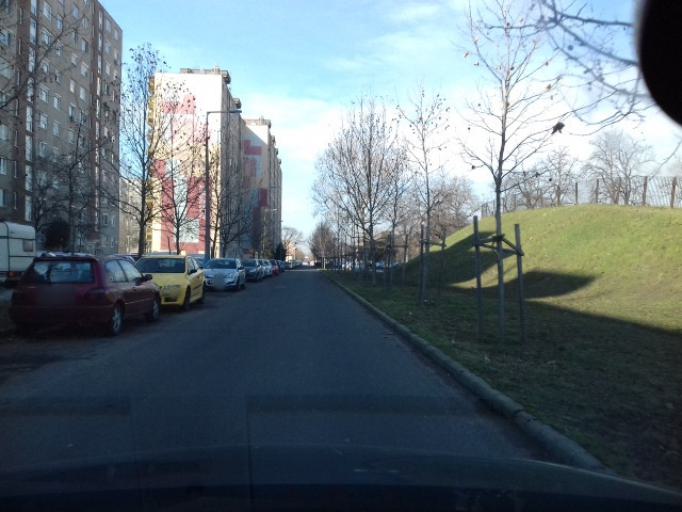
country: HU
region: Budapest
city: Budapest IV. keruelet
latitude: 47.5640
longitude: 19.0972
